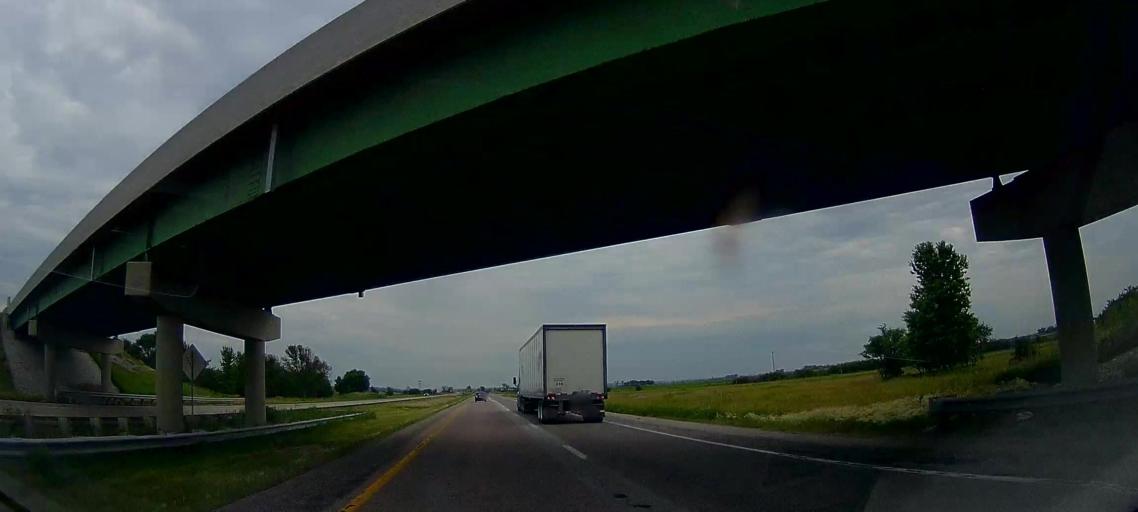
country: US
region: Iowa
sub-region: Harrison County
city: Missouri Valley
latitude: 41.6197
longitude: -95.9879
